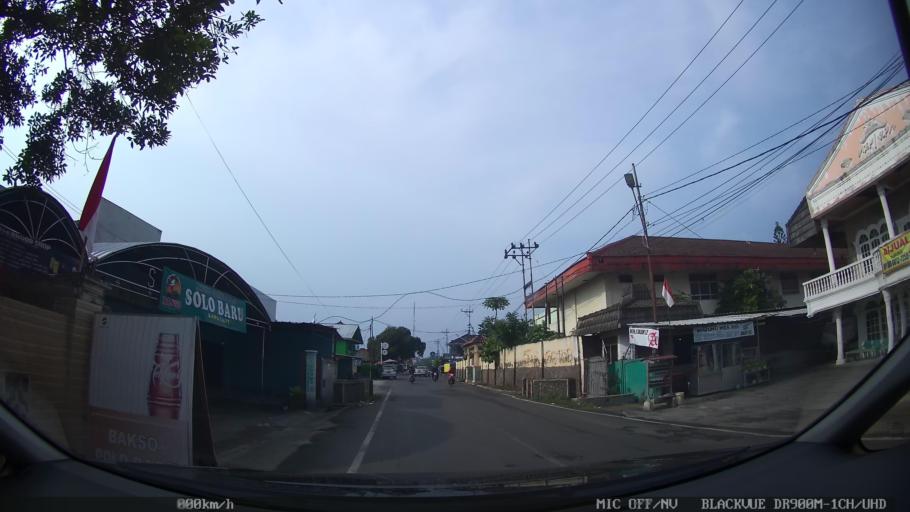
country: ID
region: Lampung
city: Bandarlampung
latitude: -5.4173
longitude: 105.2623
